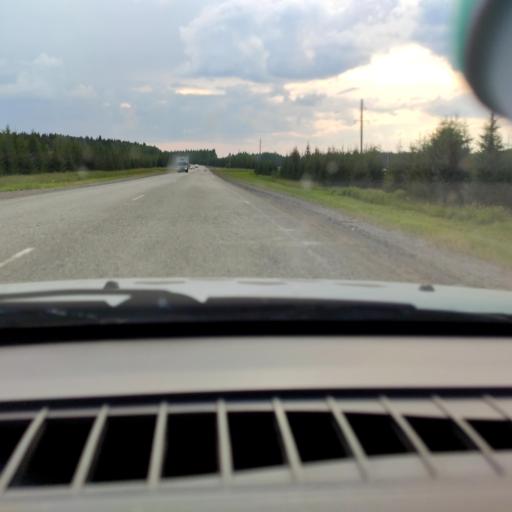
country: RU
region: Udmurtiya
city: Debesy
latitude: 57.6282
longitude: 53.7387
